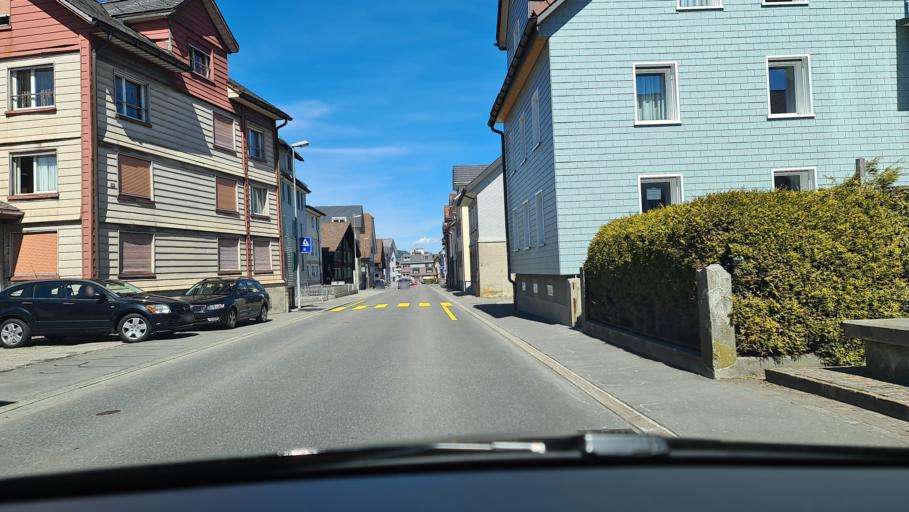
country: CH
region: Schwyz
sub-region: Bezirk Einsiedeln
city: Einsiedeln
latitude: 47.1248
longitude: 8.7434
